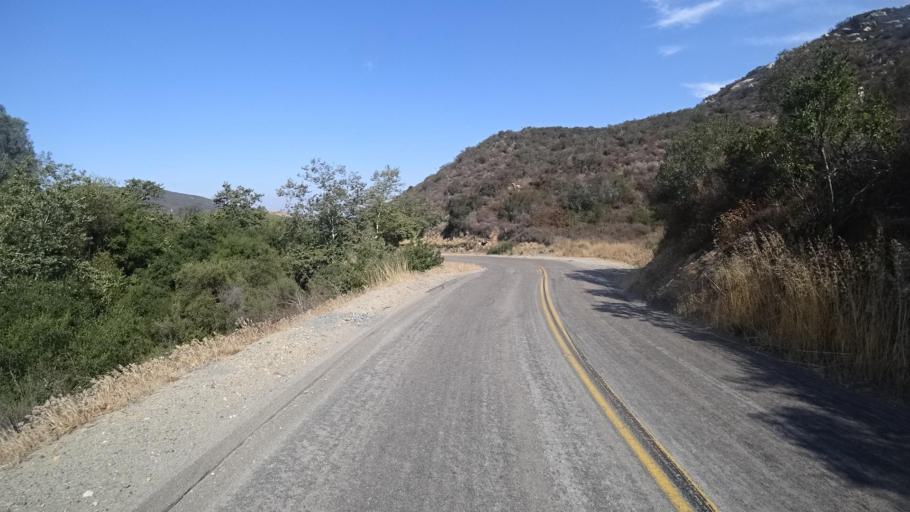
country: US
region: California
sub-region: San Diego County
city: Hidden Meadows
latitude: 33.2198
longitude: -117.1736
